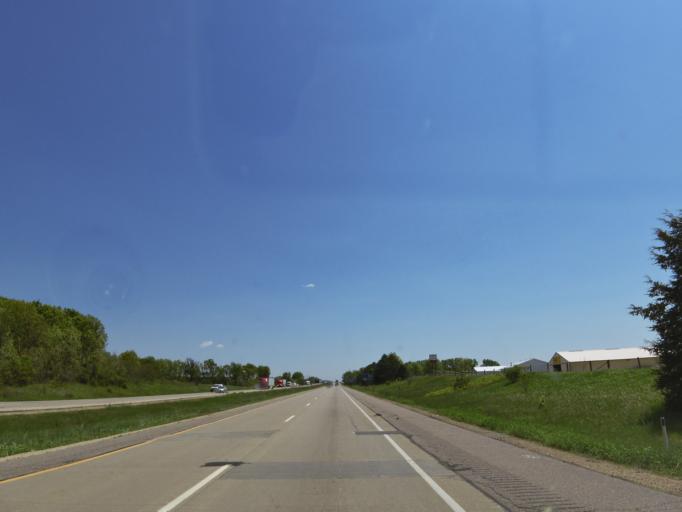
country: US
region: Wisconsin
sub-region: Juneau County
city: Mauston
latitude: 43.8096
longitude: -90.0698
